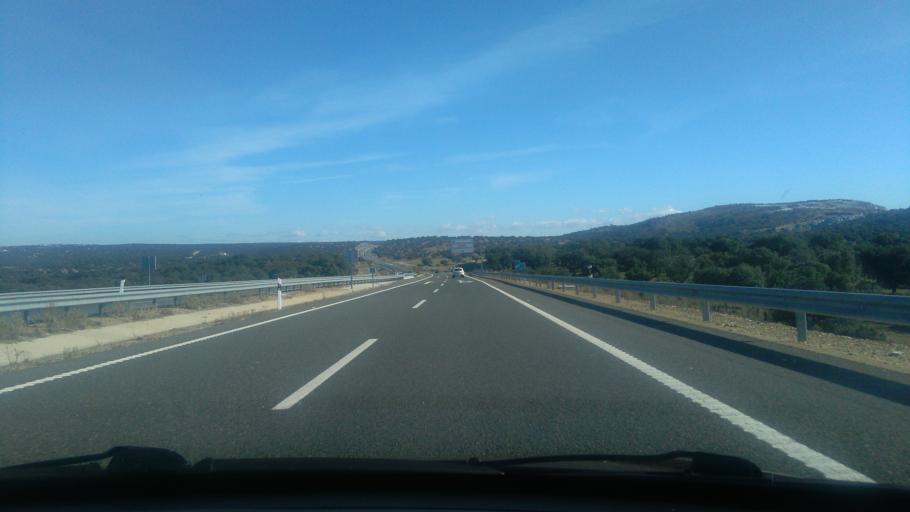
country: ES
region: Extremadura
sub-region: Provincia de Caceres
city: Plasenzuela
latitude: 39.4402
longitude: -6.0674
